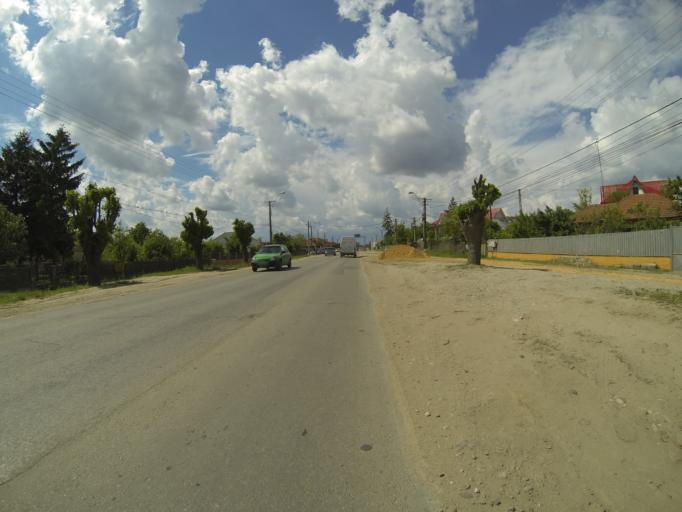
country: RO
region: Dolj
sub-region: Municipiul Craiova
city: Facai
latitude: 44.2835
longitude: 23.8029
